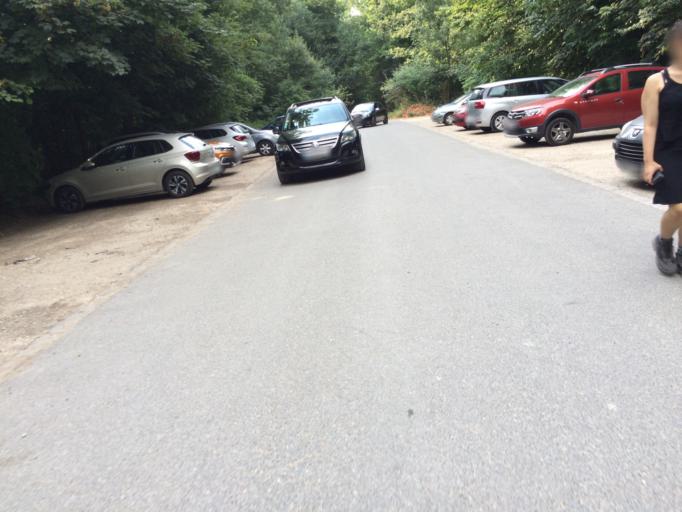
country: FR
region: Ile-de-France
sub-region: Departement des Hauts-de-Seine
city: Chatenay-Malabry
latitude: 48.7600
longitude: 2.2436
